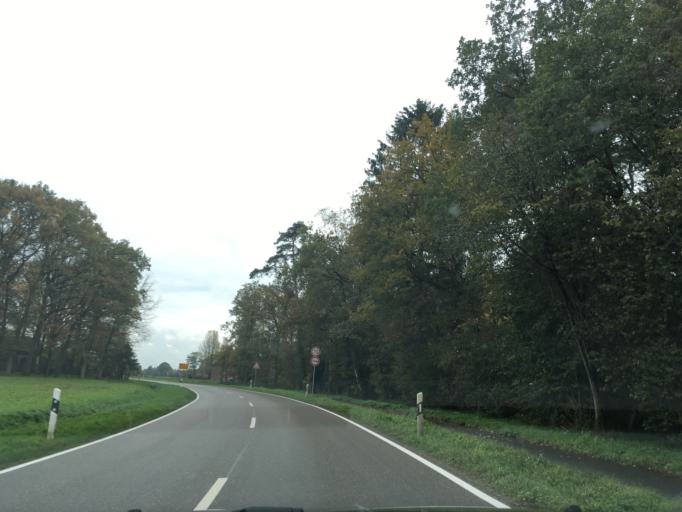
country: NL
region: Overijssel
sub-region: Gemeente Haaksbergen
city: Haaksbergen
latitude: 52.0791
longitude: 6.7591
